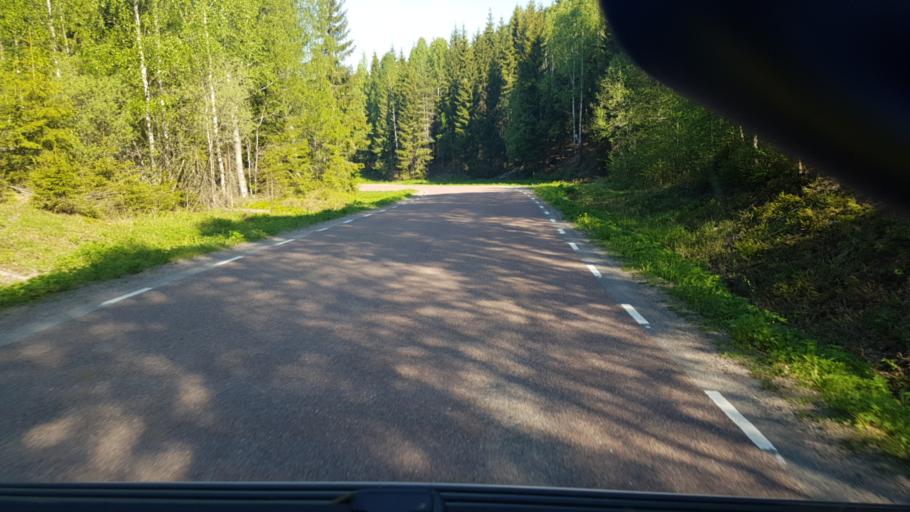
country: NO
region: Hedmark
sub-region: Eidskog
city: Skotterud
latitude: 59.8122
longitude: 12.0270
